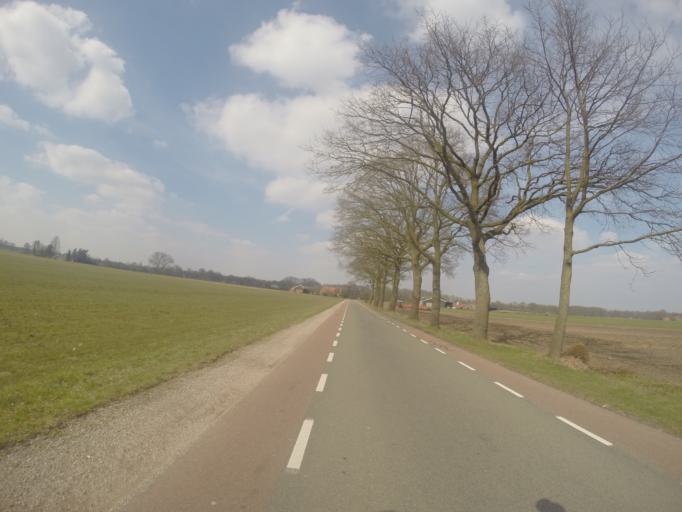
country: NL
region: Gelderland
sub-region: Gemeente Lochem
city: Almen
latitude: 52.1525
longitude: 6.3144
